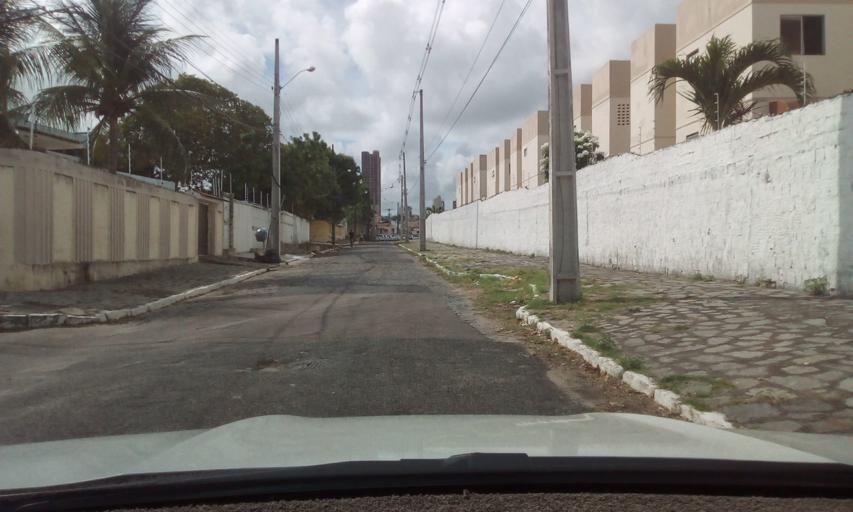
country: BR
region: Paraiba
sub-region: Joao Pessoa
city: Joao Pessoa
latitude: -7.0985
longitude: -34.8565
